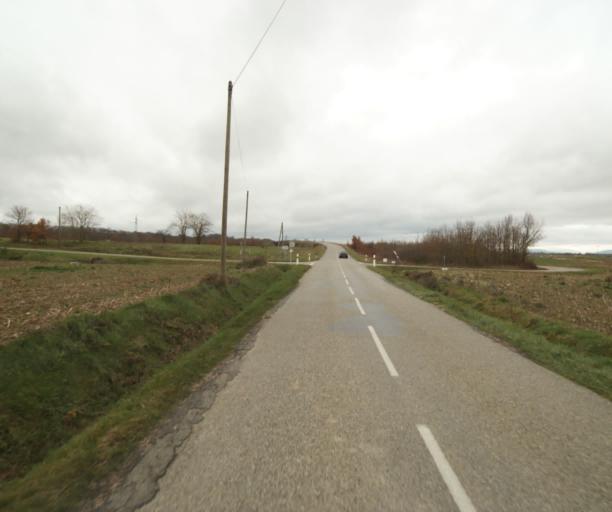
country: FR
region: Midi-Pyrenees
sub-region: Departement de l'Ariege
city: Saverdun
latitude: 43.2007
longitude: 1.6292
